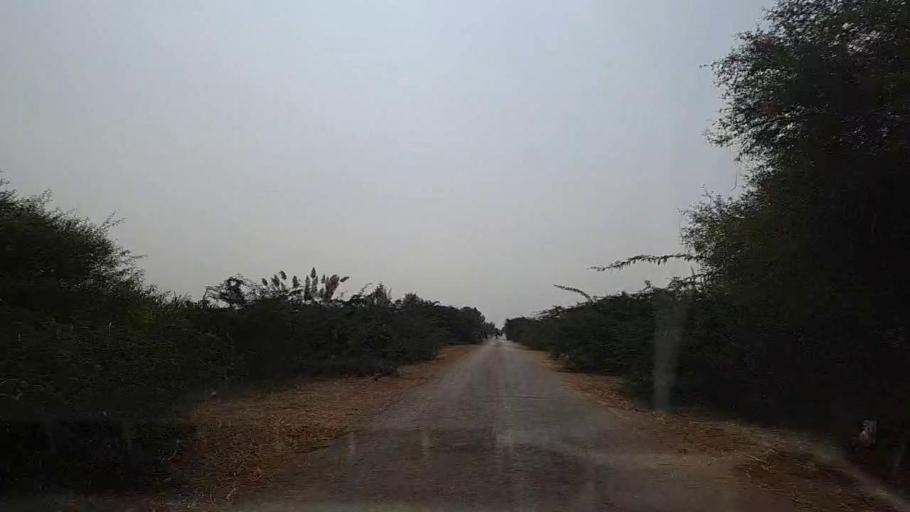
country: PK
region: Sindh
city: Chuhar Jamali
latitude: 24.2646
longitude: 67.9091
